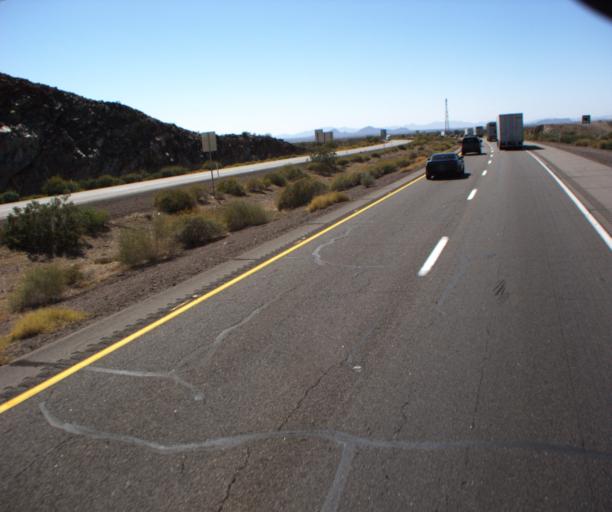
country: US
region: Arizona
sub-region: Yuma County
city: Wellton
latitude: 32.7259
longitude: -113.7507
